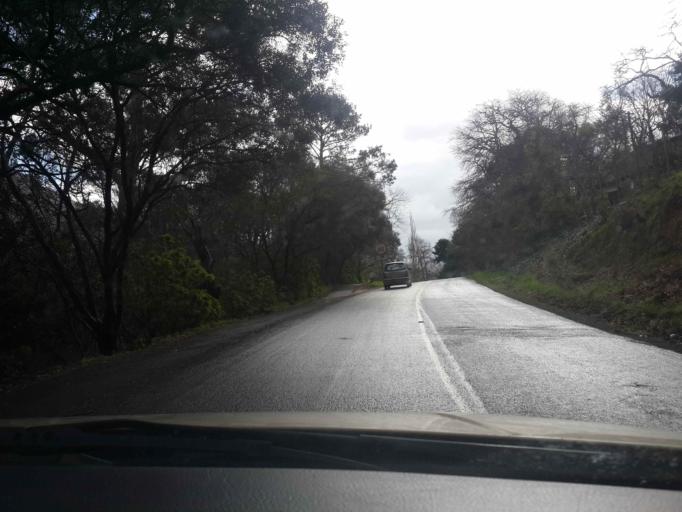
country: ZA
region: Western Cape
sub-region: Cape Winelands District Municipality
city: Stellenbosch
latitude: -33.9592
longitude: 18.9181
